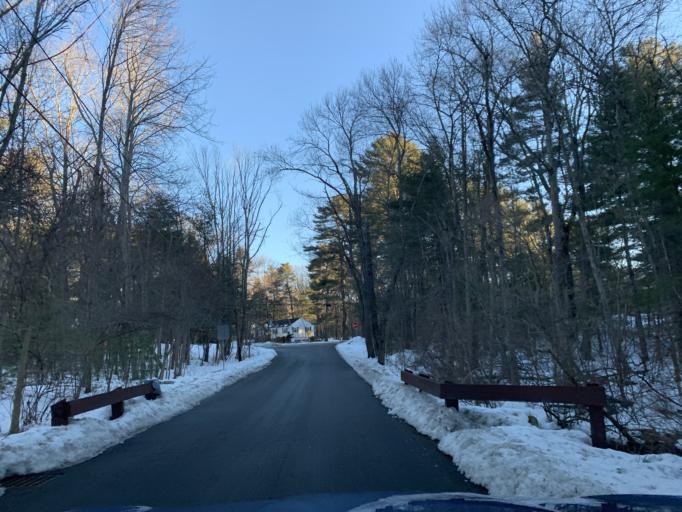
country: US
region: Massachusetts
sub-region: Norfolk County
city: Westwood
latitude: 42.2152
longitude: -71.2395
